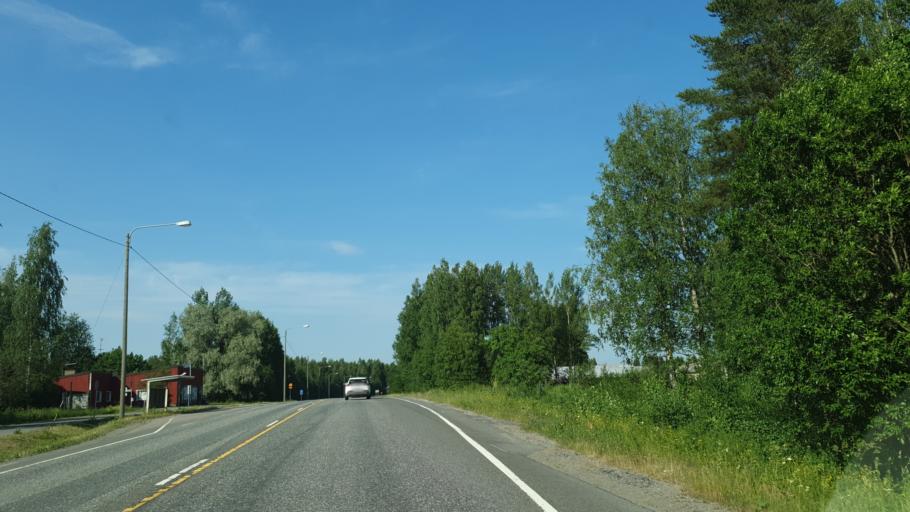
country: FI
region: Northern Savo
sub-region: Kuopio
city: Siilinjaervi
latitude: 63.1270
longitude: 27.7726
